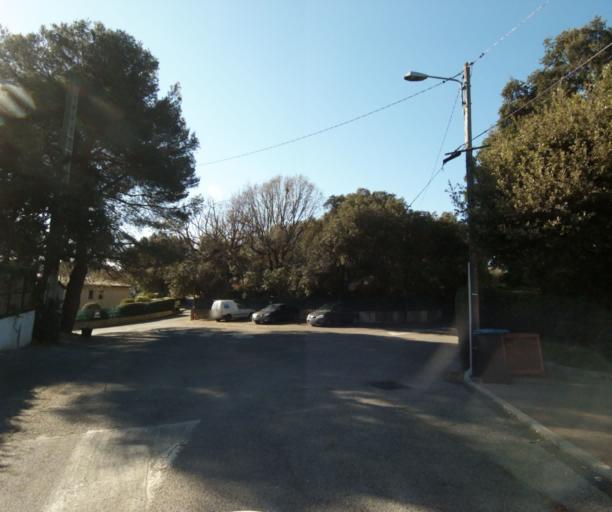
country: FR
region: Provence-Alpes-Cote d'Azur
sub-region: Departement des Alpes-Maritimes
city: Biot
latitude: 43.6113
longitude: 7.0961
